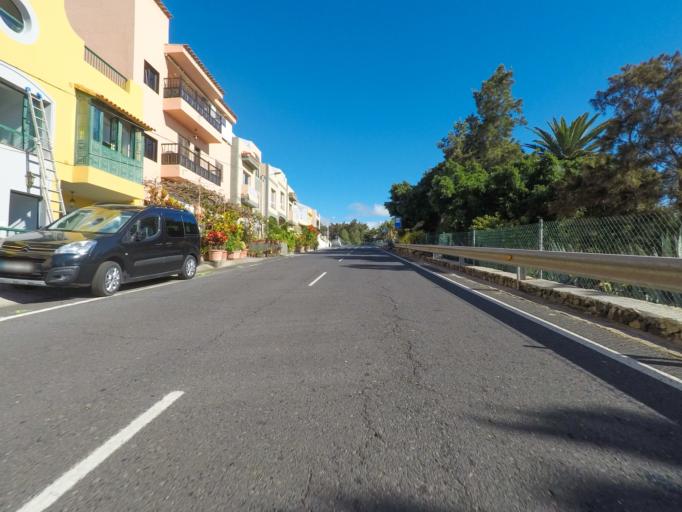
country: ES
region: Canary Islands
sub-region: Provincia de Santa Cruz de Tenerife
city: Alajero
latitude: 28.0360
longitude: -17.1906
